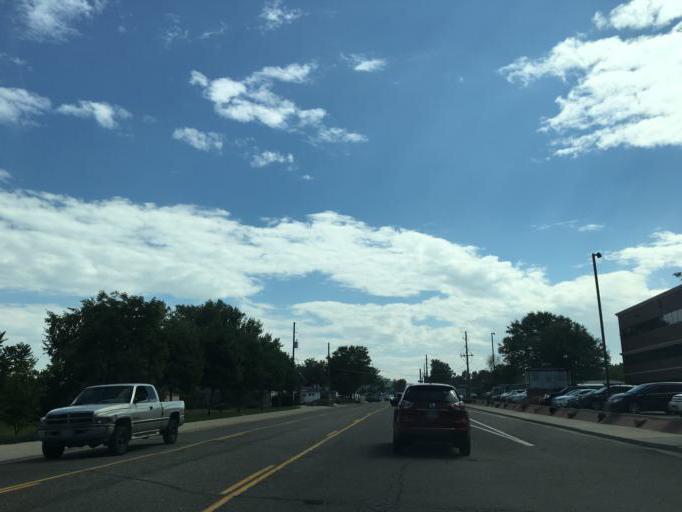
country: US
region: Colorado
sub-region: Jefferson County
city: Applewood
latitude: 39.7572
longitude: -105.1425
